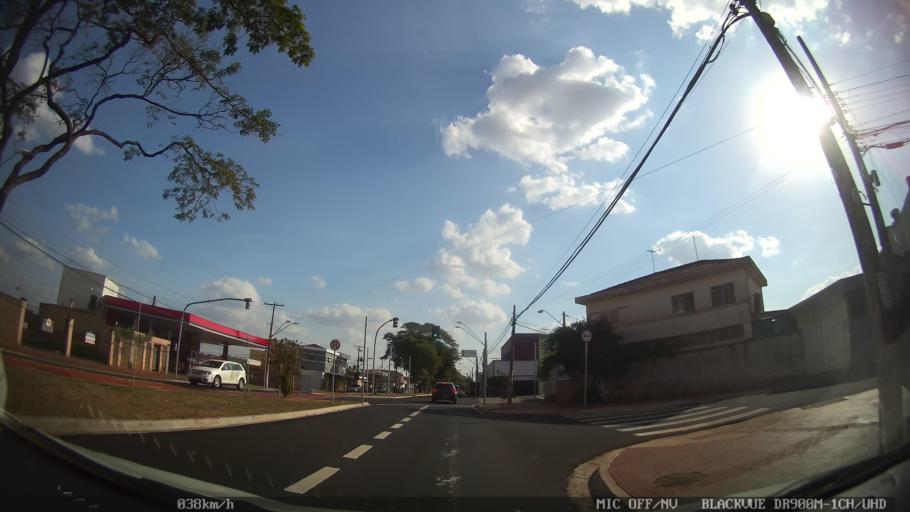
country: BR
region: Sao Paulo
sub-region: Ribeirao Preto
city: Ribeirao Preto
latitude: -21.1743
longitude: -47.8194
